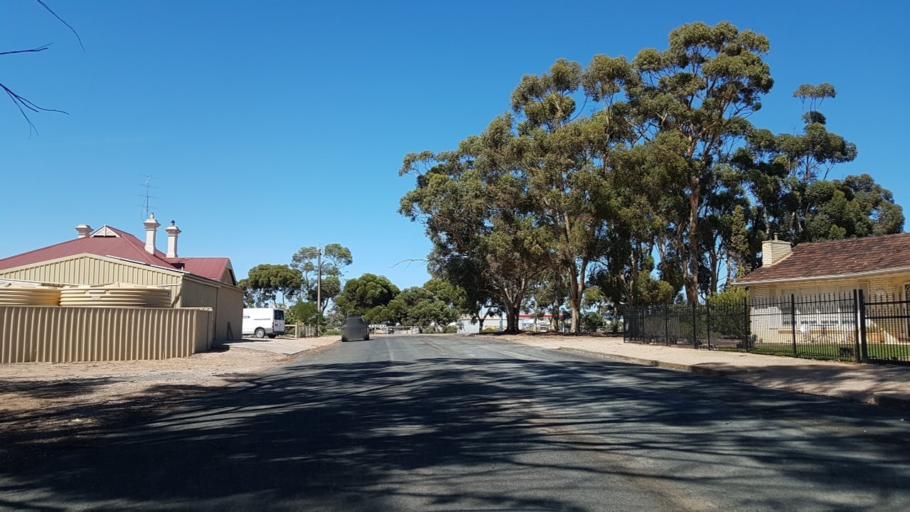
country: AU
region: South Australia
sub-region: Copper Coast
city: Kadina
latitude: -33.9653
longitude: 137.7191
